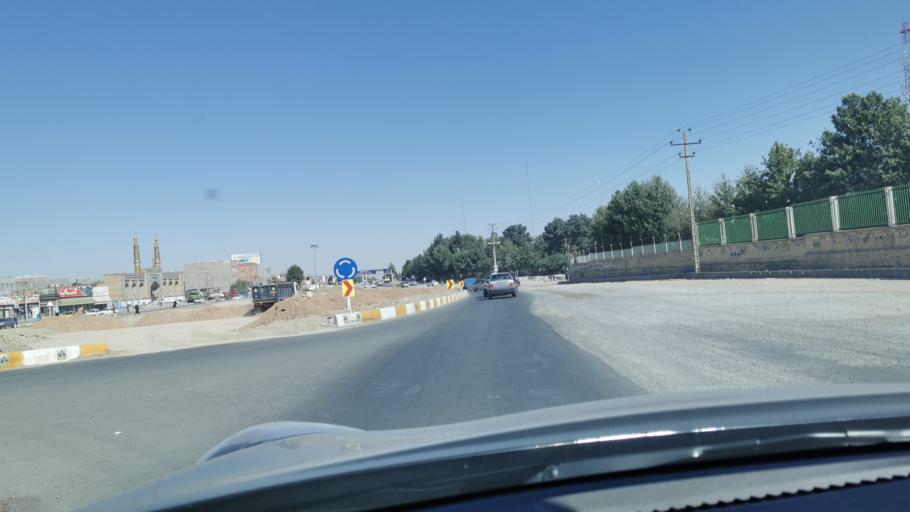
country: IR
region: Razavi Khorasan
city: Chenaran
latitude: 36.6400
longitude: 59.1197
